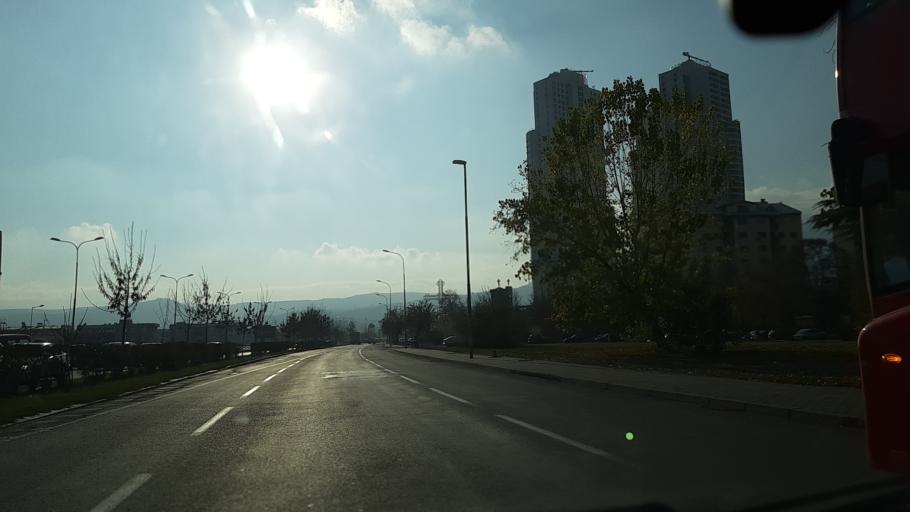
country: MK
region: Kisela Voda
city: Usje
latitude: 41.9820
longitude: 21.4705
